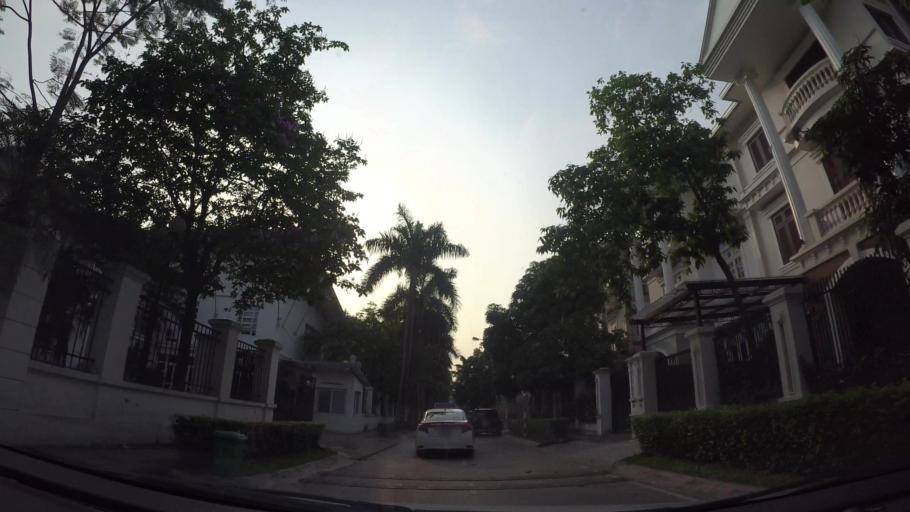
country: VN
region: Ha Noi
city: Tay Ho
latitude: 21.0755
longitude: 105.8025
